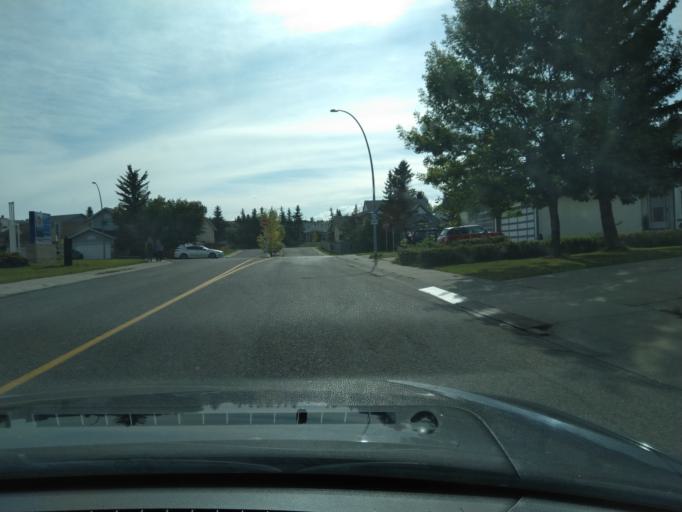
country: CA
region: Alberta
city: Calgary
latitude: 51.1388
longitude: -114.1005
